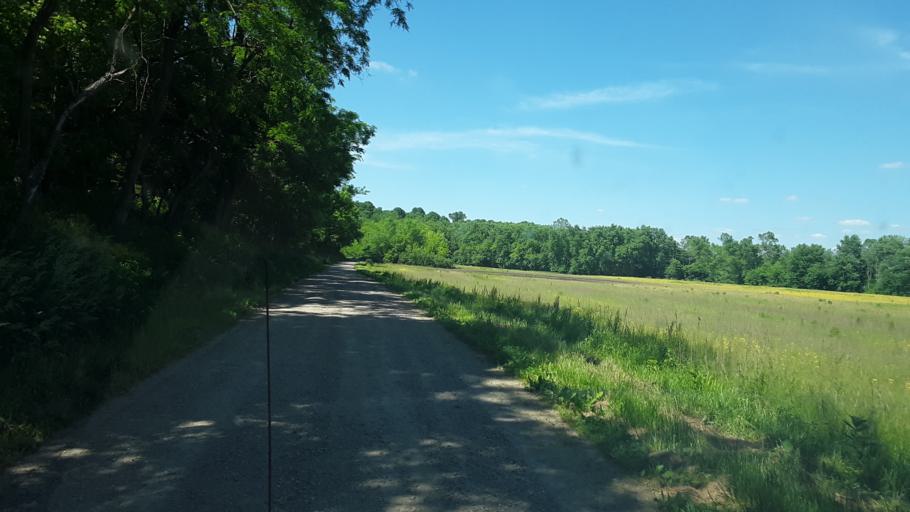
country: US
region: Ohio
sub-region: Coshocton County
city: West Lafayette
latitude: 40.1937
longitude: -81.6903
